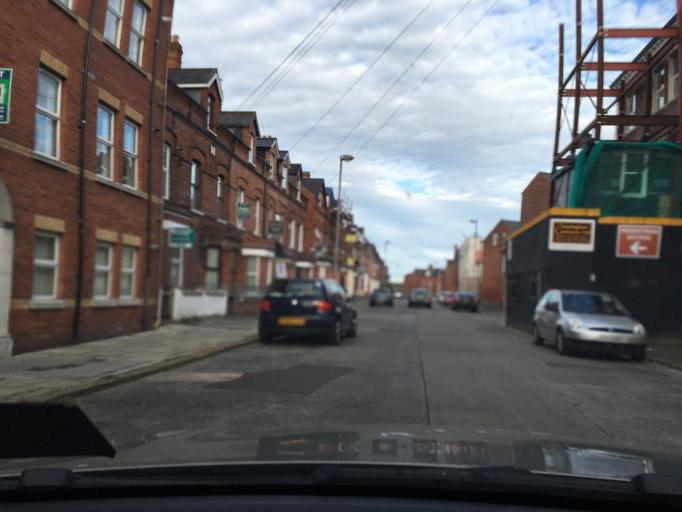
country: GB
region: Northern Ireland
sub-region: City of Belfast
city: Belfast
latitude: 54.5877
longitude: -5.9301
